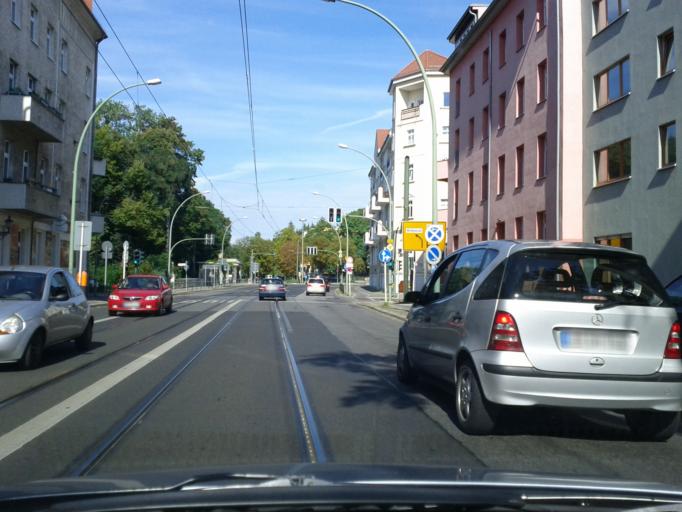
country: DE
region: Berlin
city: Pankow
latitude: 52.5703
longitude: 13.3995
